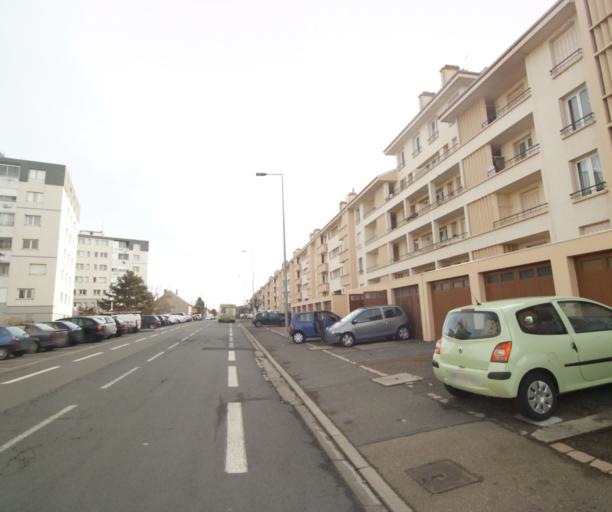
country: FR
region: Rhone-Alpes
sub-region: Departement de la Loire
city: Riorges
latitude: 46.0242
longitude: 4.0496
